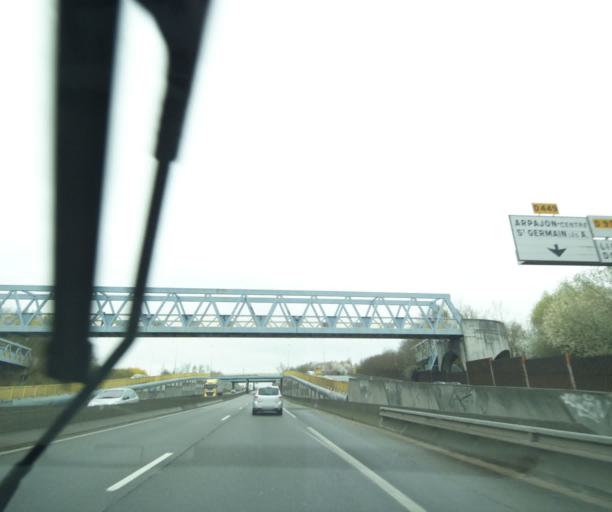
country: FR
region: Ile-de-France
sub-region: Departement de l'Essonne
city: Arpajon
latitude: 48.6000
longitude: 2.2461
